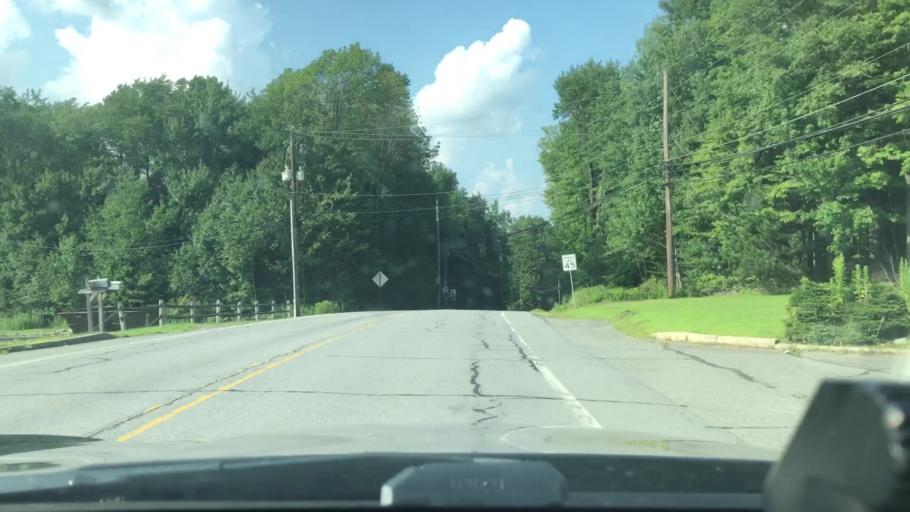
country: US
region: Pennsylvania
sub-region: Lackawanna County
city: Moscow
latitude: 41.2865
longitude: -75.5111
